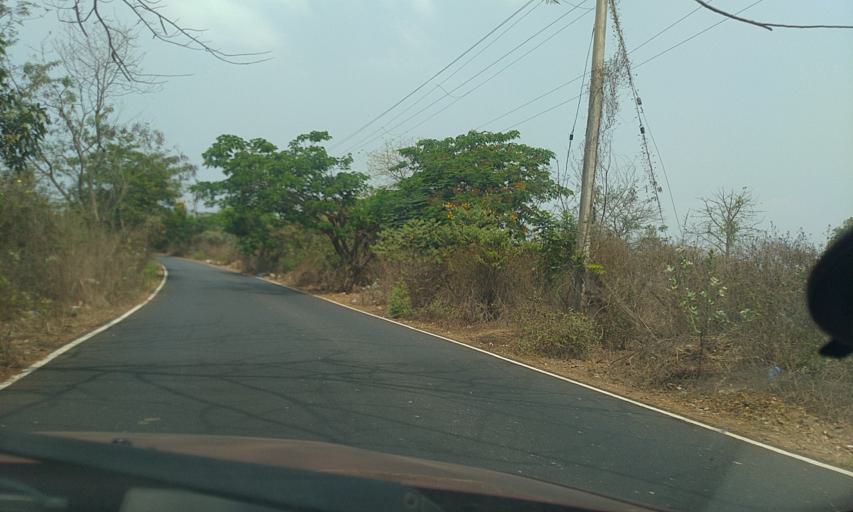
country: IN
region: Goa
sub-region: North Goa
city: Mapuca
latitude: 15.6083
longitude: 73.7998
